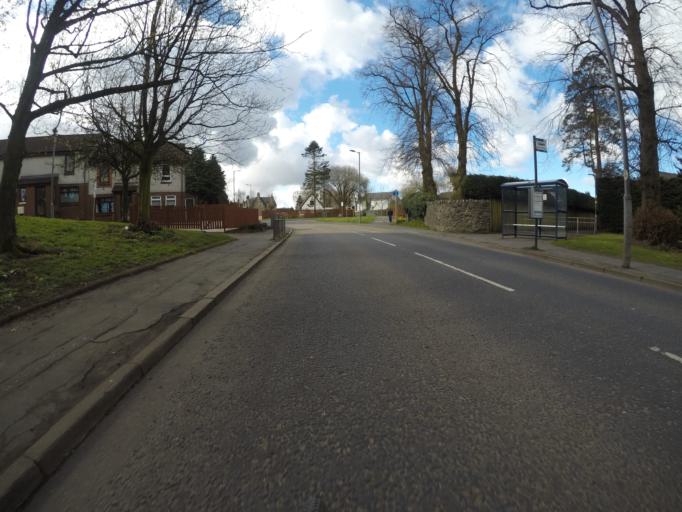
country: GB
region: Scotland
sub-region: North Ayrshire
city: Beith
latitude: 55.7462
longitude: -4.6400
